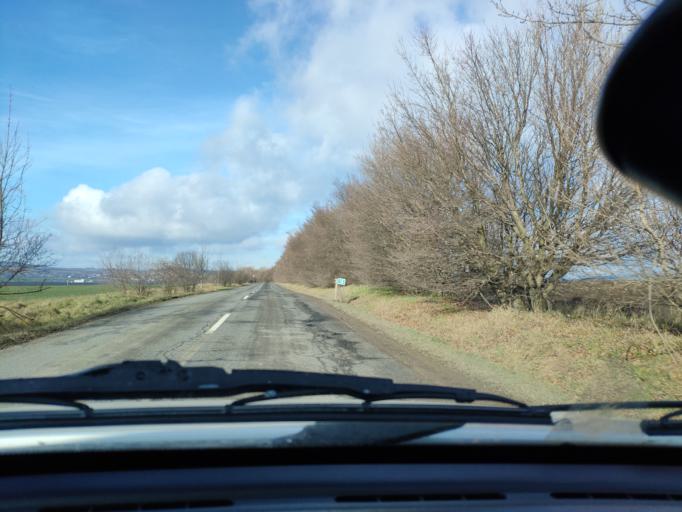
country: HU
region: Pest
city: Perbal
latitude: 47.5685
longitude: 18.7899
